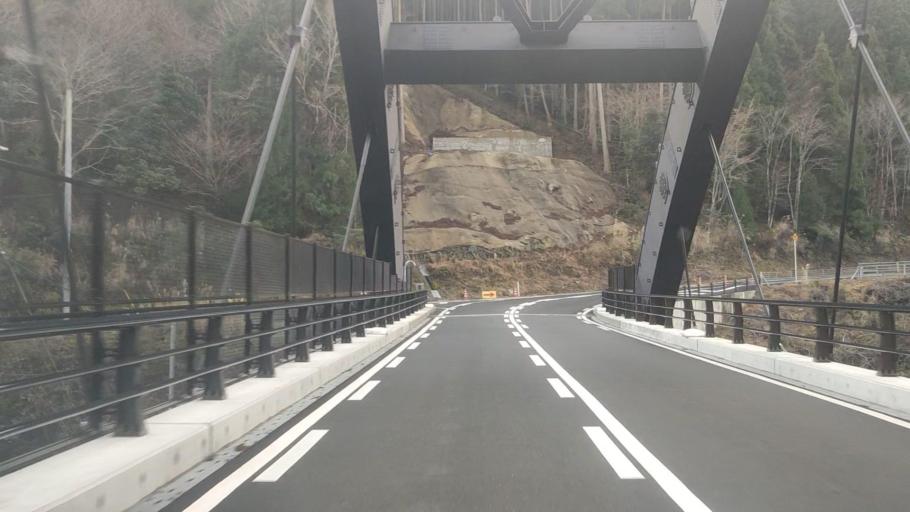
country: JP
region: Kumamoto
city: Hitoyoshi
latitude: 32.4109
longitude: 130.8401
